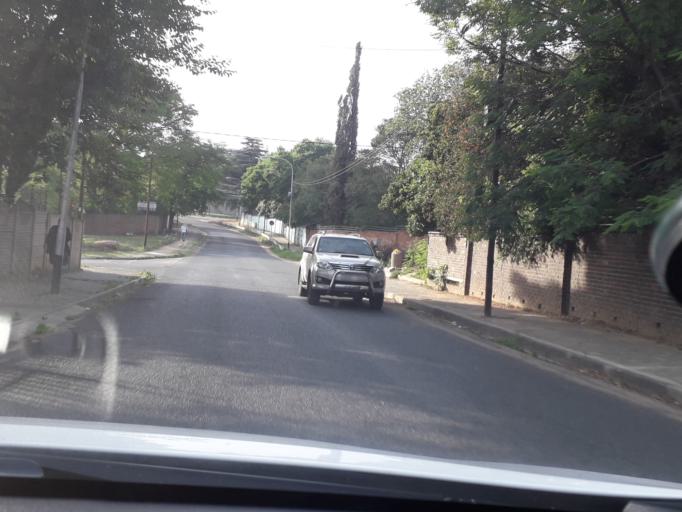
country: ZA
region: Gauteng
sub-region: City of Johannesburg Metropolitan Municipality
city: Modderfontein
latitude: -26.1299
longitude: 28.1042
